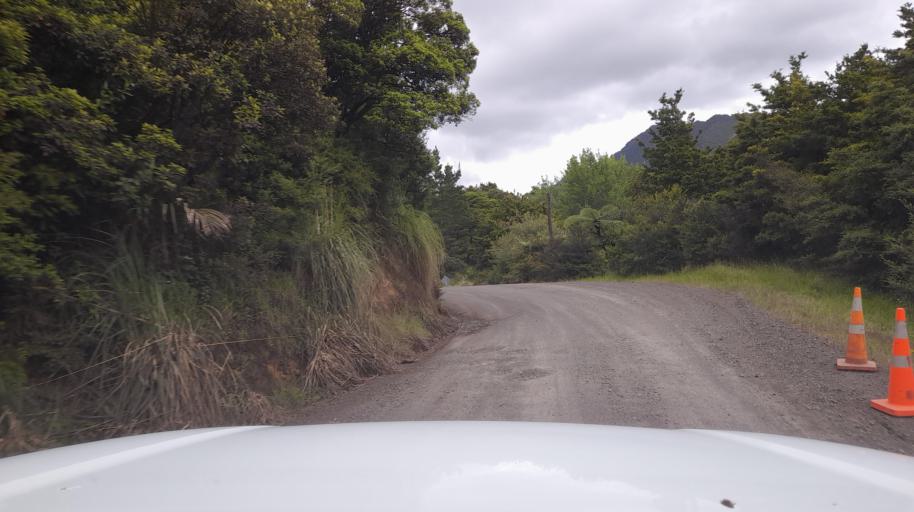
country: NZ
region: Northland
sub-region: Far North District
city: Kaitaia
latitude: -35.3231
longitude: 173.3512
